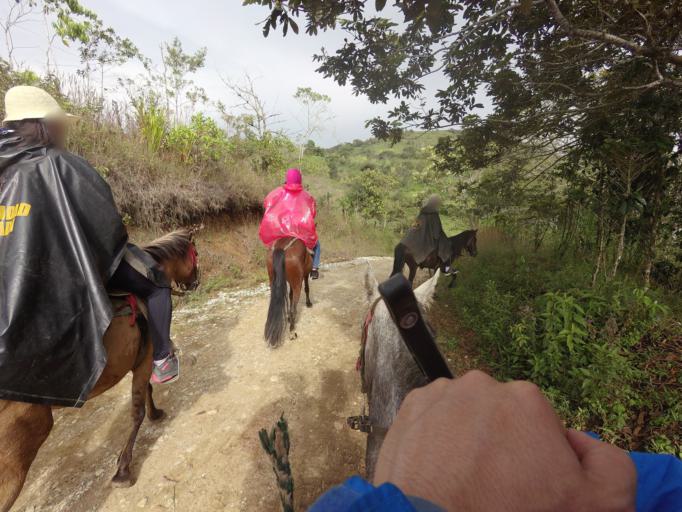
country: CO
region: Huila
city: San Agustin
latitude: 1.9090
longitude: -76.2931
